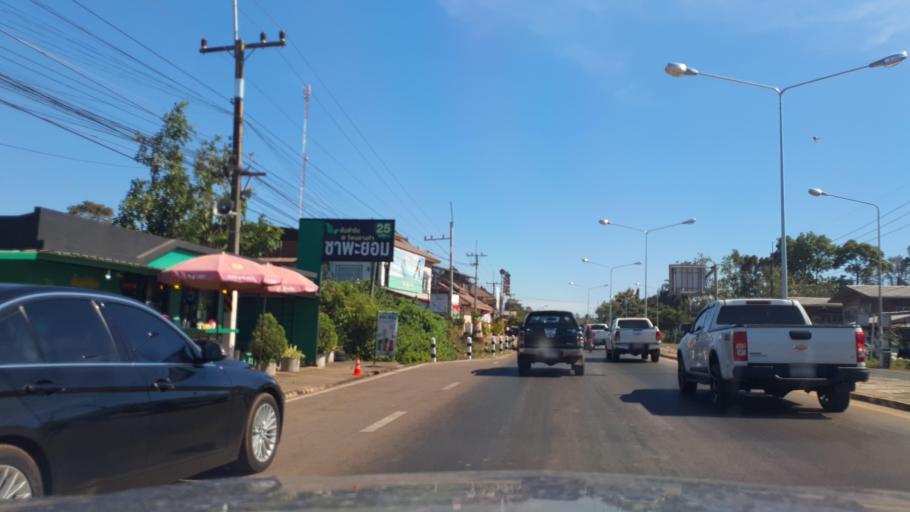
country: TH
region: Sakon Nakhon
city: Tao Ngoi
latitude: 17.0827
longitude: 104.1915
